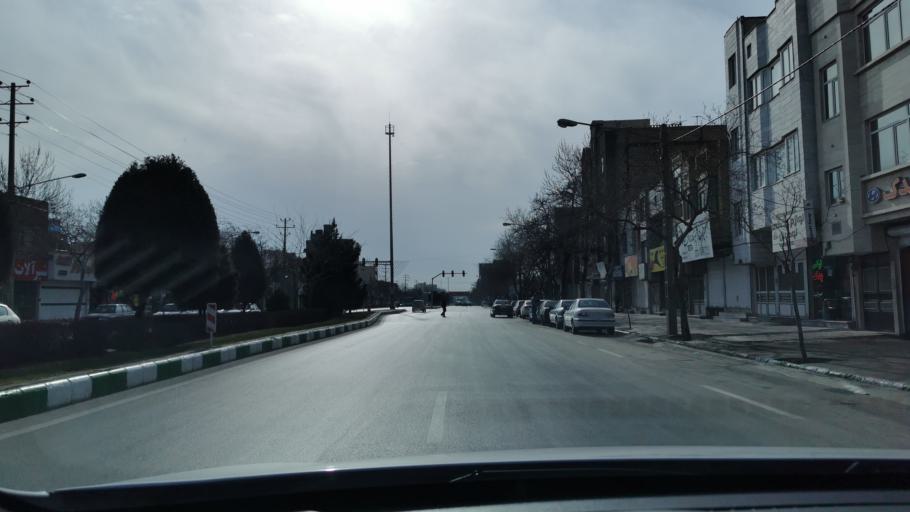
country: IR
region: Razavi Khorasan
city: Mashhad
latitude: 36.2993
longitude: 59.5237
